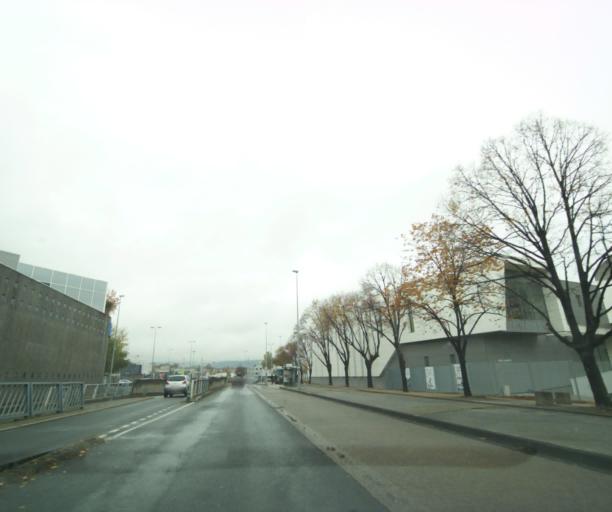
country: FR
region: Auvergne
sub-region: Departement du Puy-de-Dome
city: Aubiere
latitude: 45.7622
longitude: 3.1301
